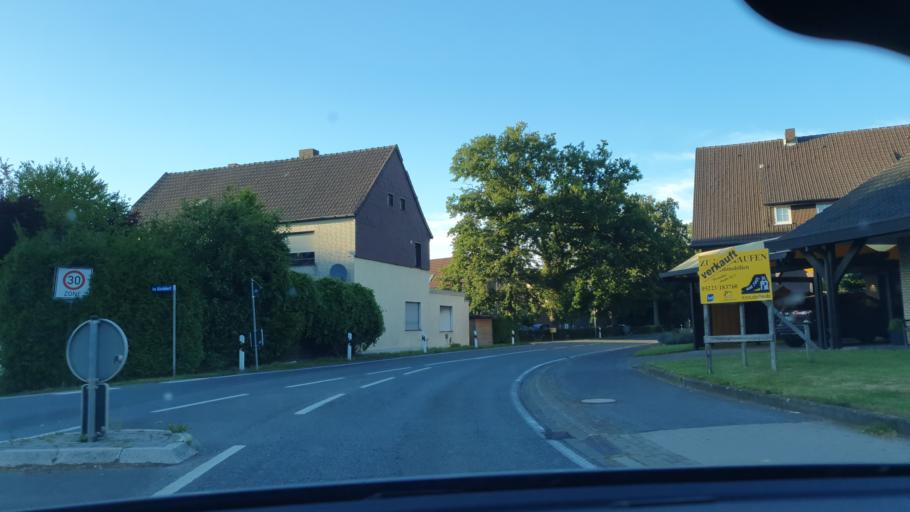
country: DE
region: North Rhine-Westphalia
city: Spenge
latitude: 52.1728
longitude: 8.5077
